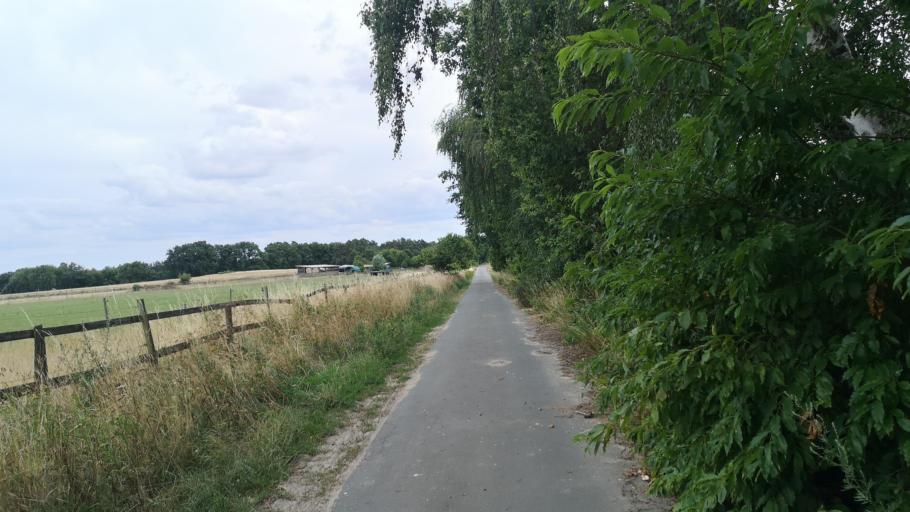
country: DE
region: Lower Saxony
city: Thomasburg
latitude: 53.2302
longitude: 10.6973
